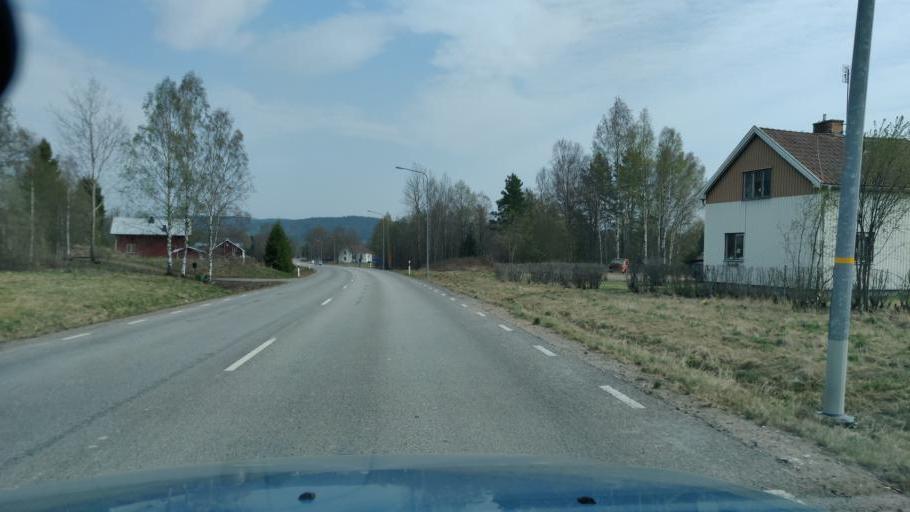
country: SE
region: Vaermland
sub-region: Munkfors Kommun
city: Munkfors
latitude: 59.8323
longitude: 13.5120
